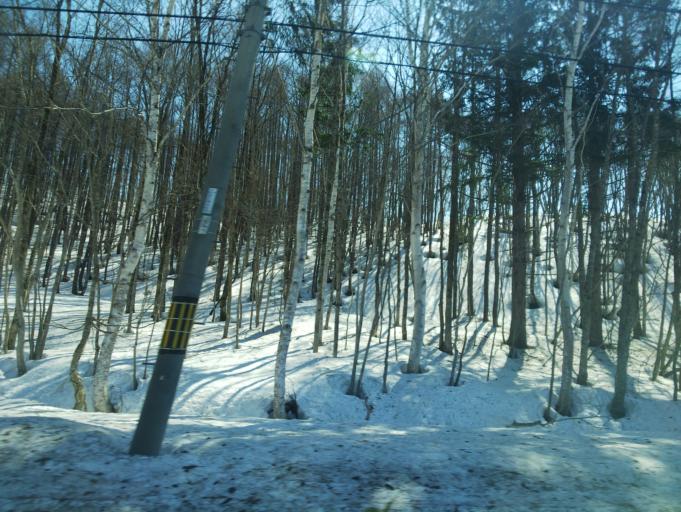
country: JP
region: Hokkaido
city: Nayoro
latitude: 44.6936
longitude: 142.2697
